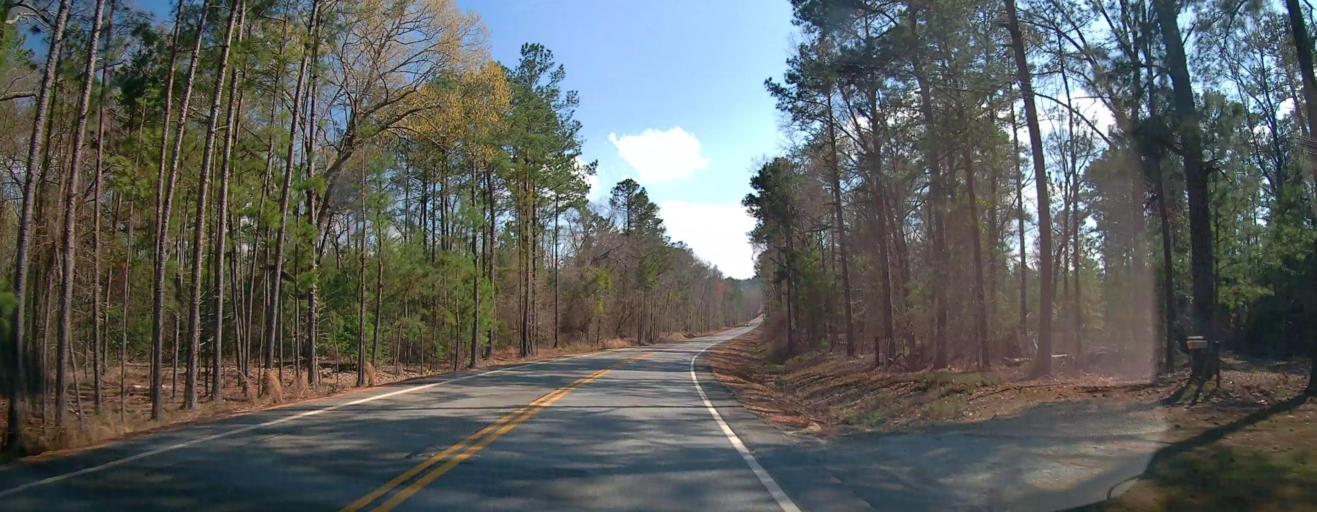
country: US
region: Georgia
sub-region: Wilkinson County
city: Gordon
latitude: 32.8218
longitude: -83.3254
